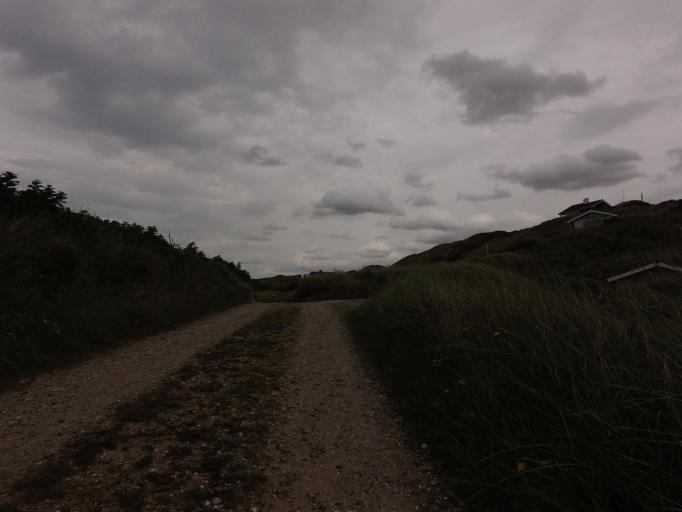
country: DK
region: North Denmark
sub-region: Jammerbugt Kommune
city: Pandrup
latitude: 57.3119
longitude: 9.6504
